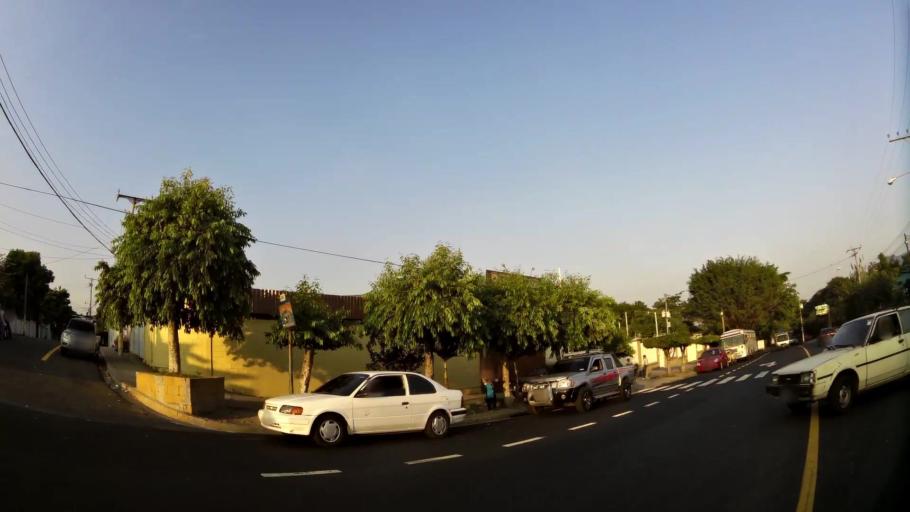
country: SV
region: San Salvador
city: San Salvador
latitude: 13.6850
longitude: -89.2125
